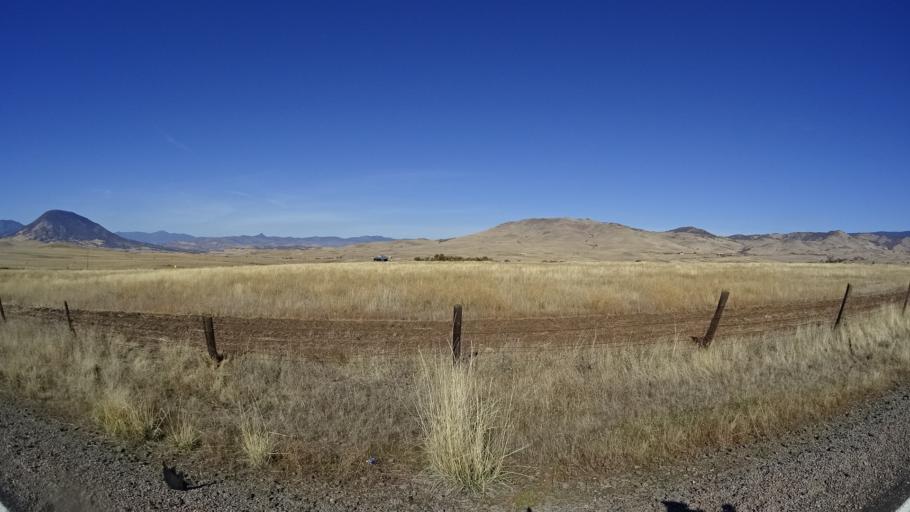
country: US
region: California
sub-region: Siskiyou County
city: Montague
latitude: 41.8043
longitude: -122.4137
